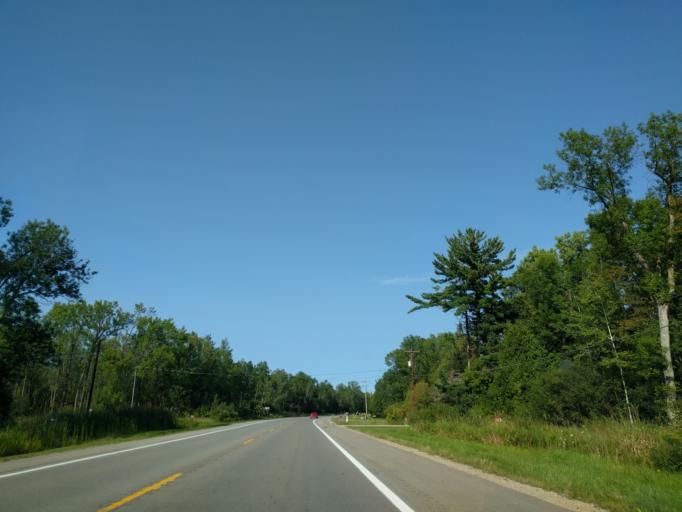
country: US
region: Michigan
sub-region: Menominee County
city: Menominee
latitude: 45.1660
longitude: -87.5873
